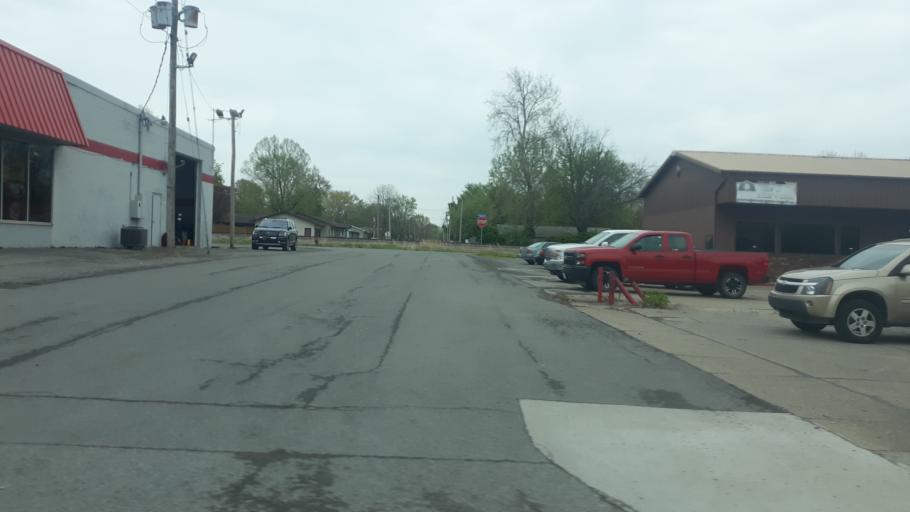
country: US
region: Illinois
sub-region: Williamson County
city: Marion
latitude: 37.7383
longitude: -88.9325
